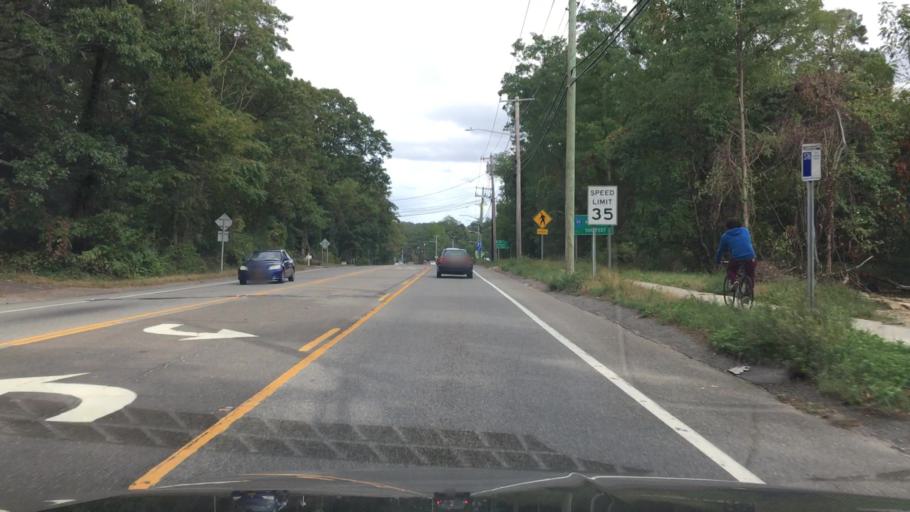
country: US
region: New York
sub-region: Suffolk County
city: Stony Brook
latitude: 40.9249
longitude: -73.1235
